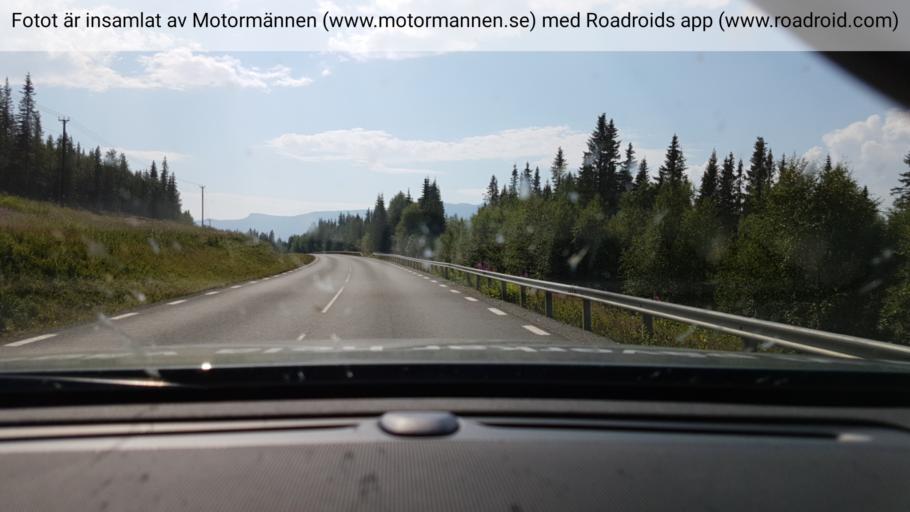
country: SE
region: Vaesterbotten
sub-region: Vilhelmina Kommun
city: Sjoberg
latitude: 65.5772
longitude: 15.5299
